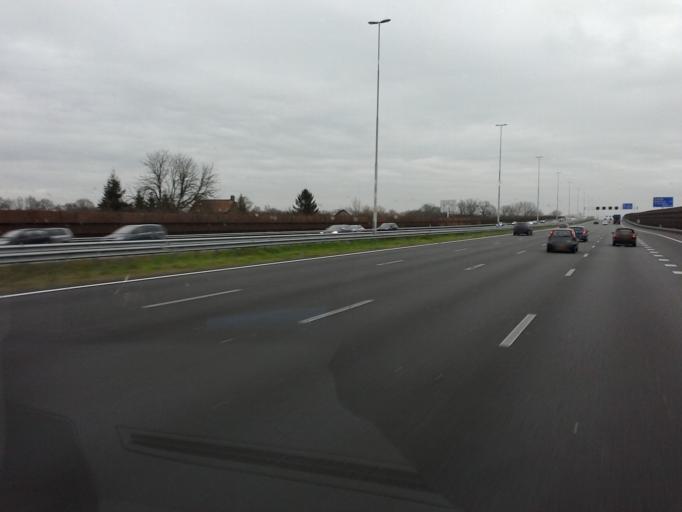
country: NL
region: Gelderland
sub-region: Gemeente Culemborg
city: Culemborg
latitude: 51.8935
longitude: 5.1957
